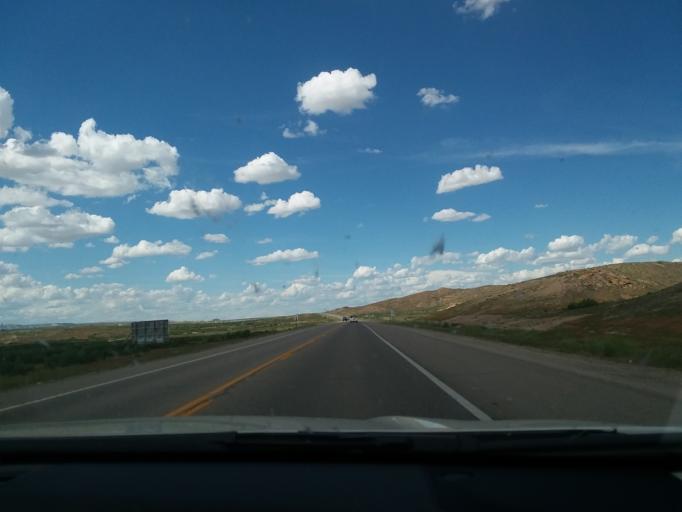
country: US
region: Wyoming
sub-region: Sweetwater County
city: North Rock Springs
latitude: 41.6330
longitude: -109.2309
